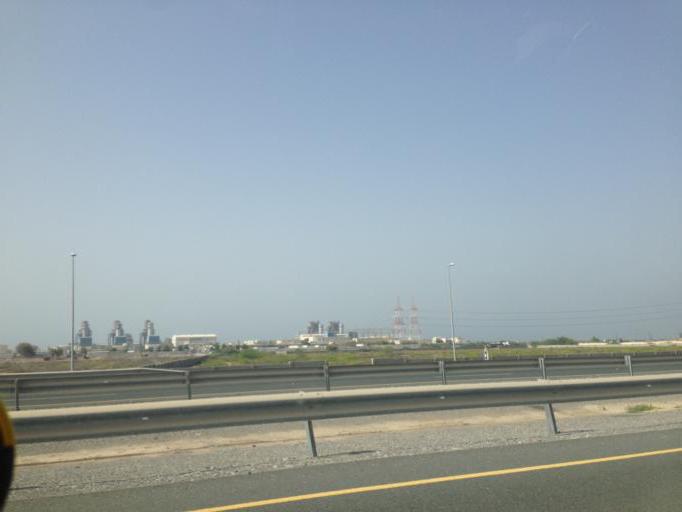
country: OM
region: Al Batinah
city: Barka'
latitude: 23.6990
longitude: 57.9816
